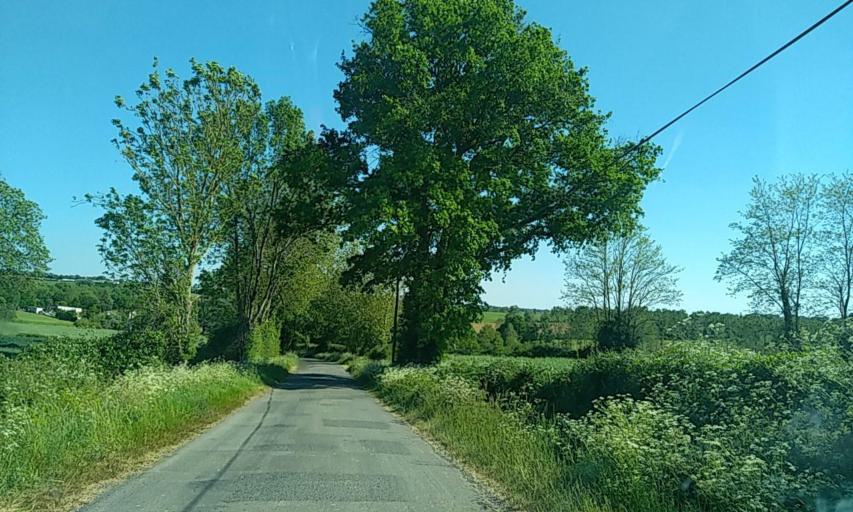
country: FR
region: Poitou-Charentes
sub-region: Departement des Deux-Sevres
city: Boisme
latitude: 46.7754
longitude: -0.4145
